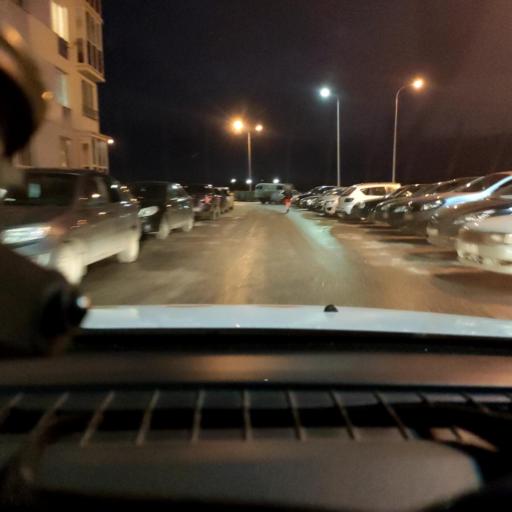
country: RU
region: Samara
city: Samara
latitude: 53.0935
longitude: 50.1584
